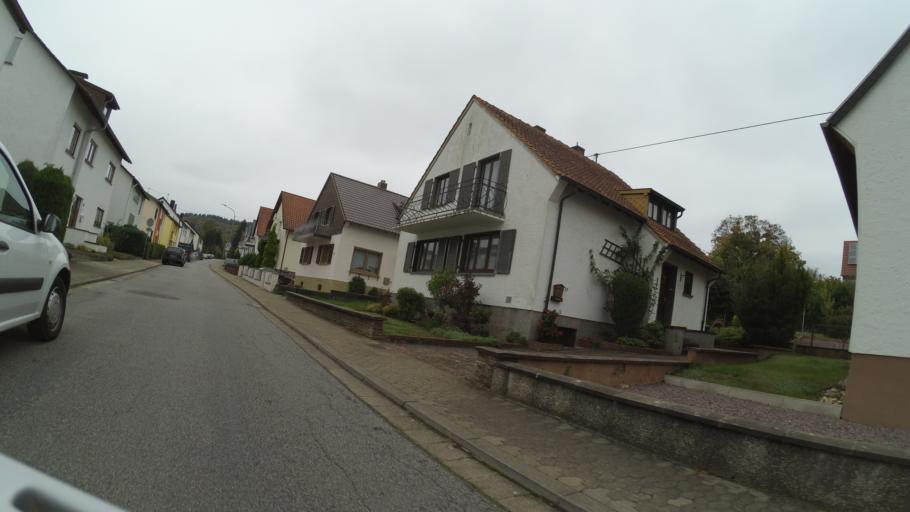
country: DE
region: Saarland
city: Blieskastel
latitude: 49.2633
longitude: 7.2790
